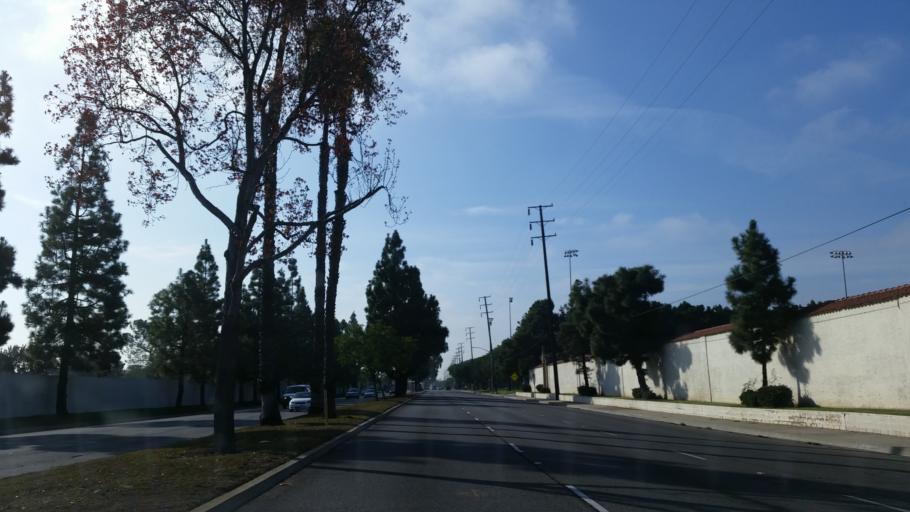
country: US
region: California
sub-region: Los Angeles County
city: Lakewood
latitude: 33.8418
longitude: -118.1676
